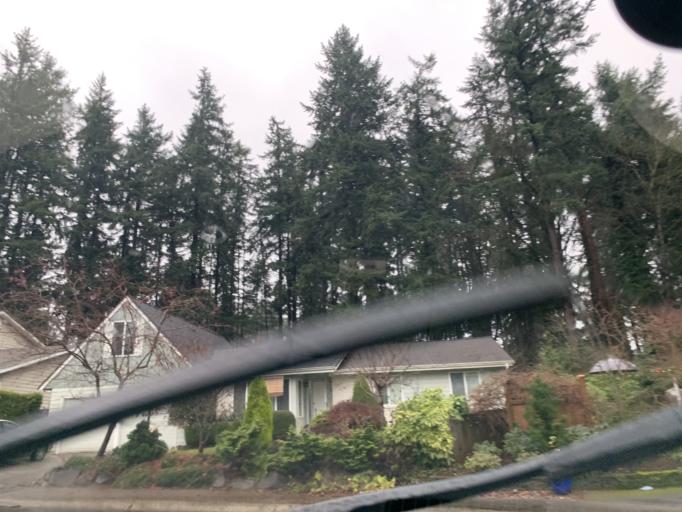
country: US
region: Washington
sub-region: King County
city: Kingsgate
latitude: 47.7383
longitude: -122.1815
